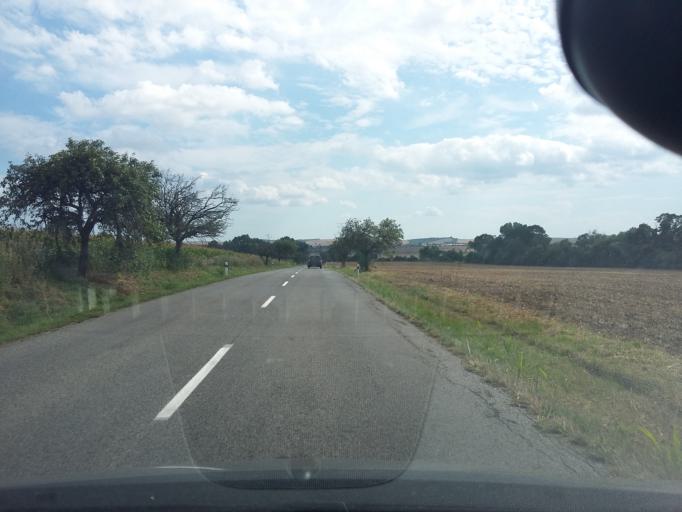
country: SK
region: Trnavsky
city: Gbely
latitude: 48.7488
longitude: 17.1706
